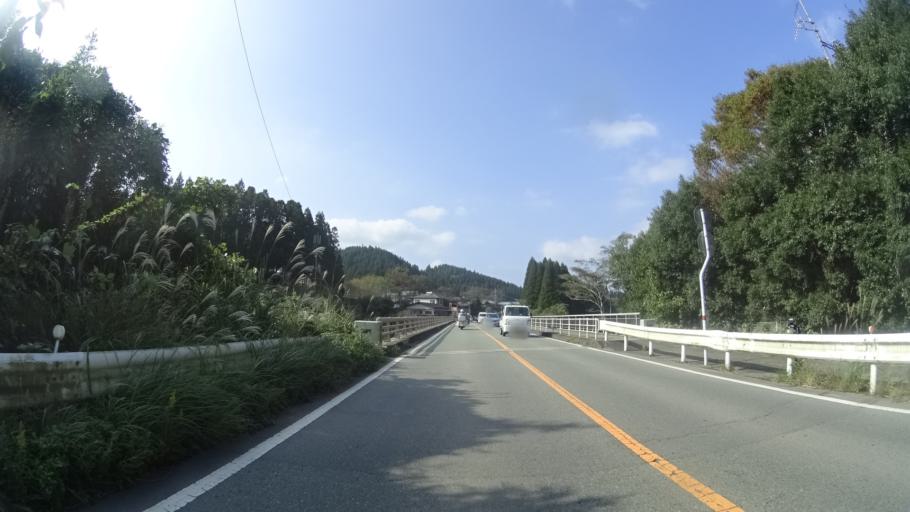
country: JP
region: Kumamoto
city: Aso
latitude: 33.1121
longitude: 131.0616
